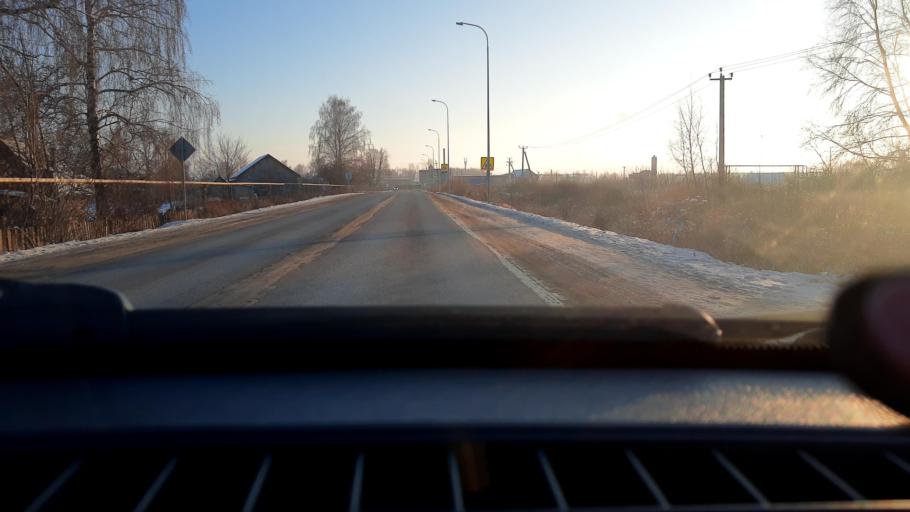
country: RU
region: Bashkortostan
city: Iglino
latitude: 54.8325
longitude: 56.3908
